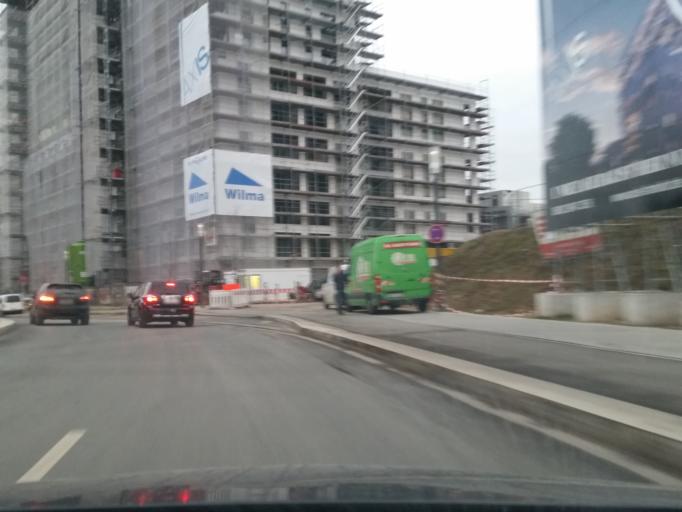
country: DE
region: Hesse
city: Niederrad
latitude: 50.1076
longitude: 8.6226
